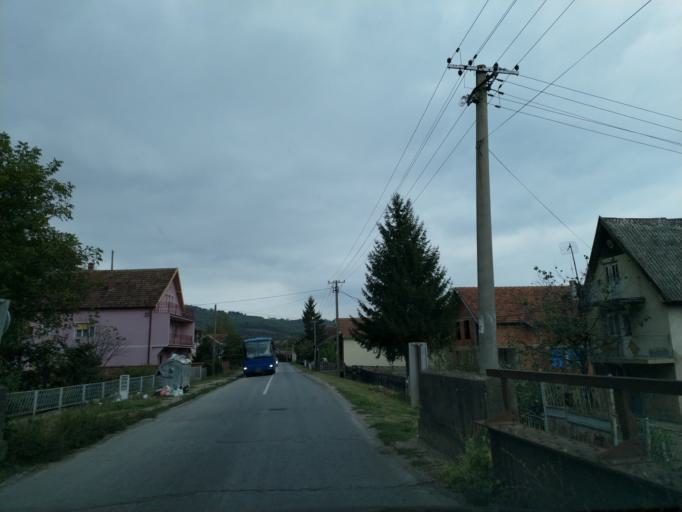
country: RS
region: Central Serbia
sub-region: Pomoravski Okrug
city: Jagodina
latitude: 44.0658
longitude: 21.1806
